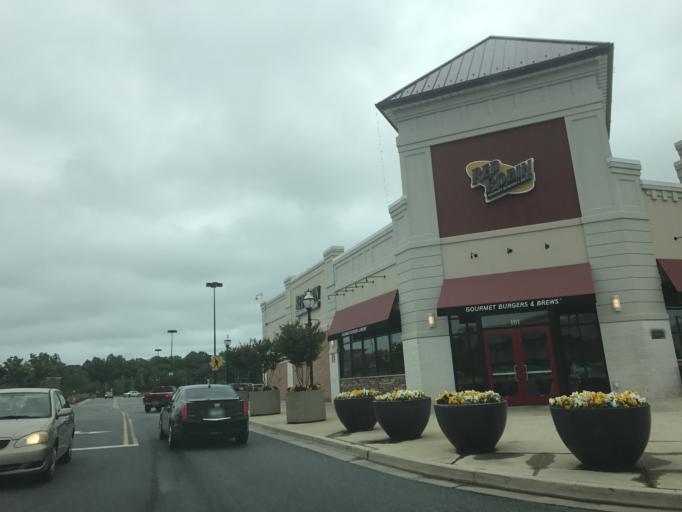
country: US
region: Maryland
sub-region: Anne Arundel County
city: Crofton
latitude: 39.0321
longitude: -76.6850
